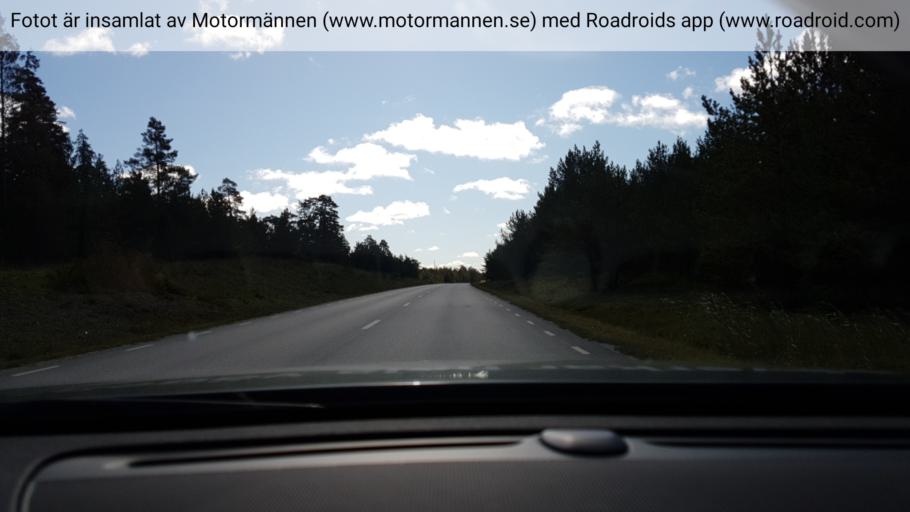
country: SE
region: Gotland
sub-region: Gotland
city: Slite
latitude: 57.7390
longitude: 18.7906
